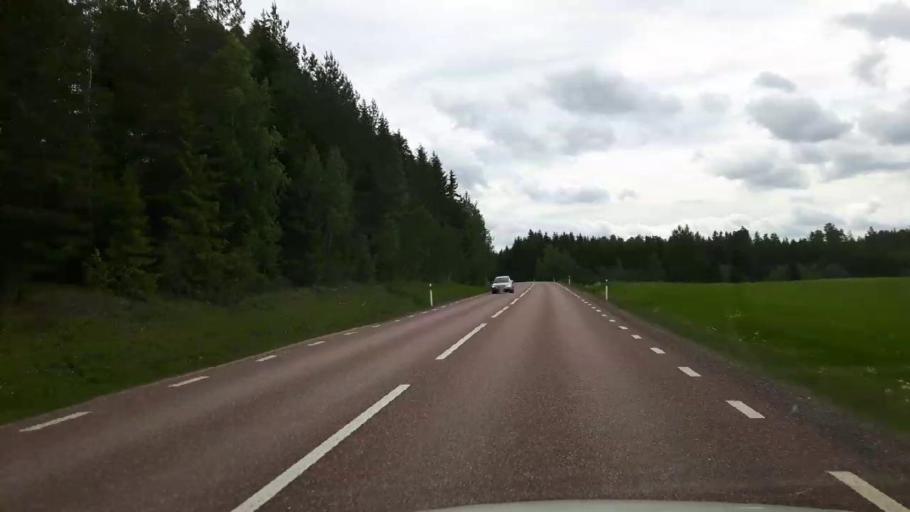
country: SE
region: Dalarna
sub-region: Hedemora Kommun
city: Brunna
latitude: 60.2102
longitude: 15.9917
